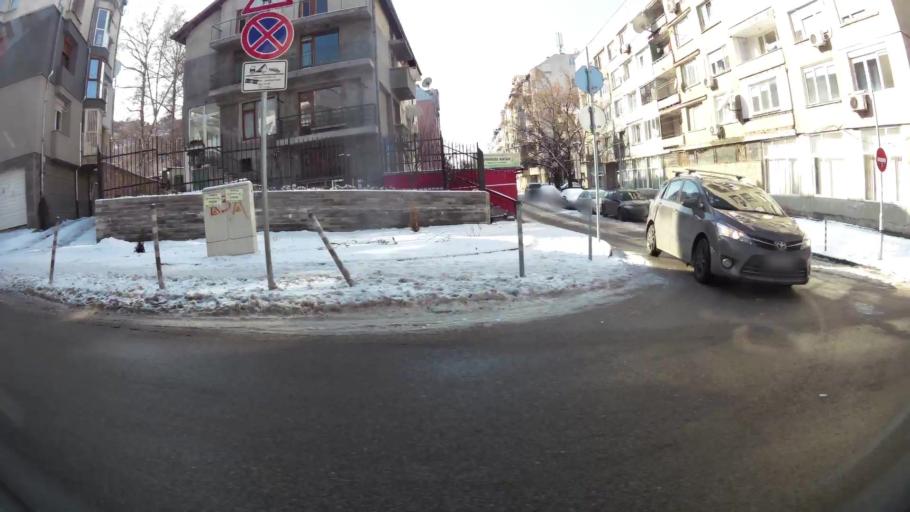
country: BG
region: Sofia-Capital
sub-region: Stolichna Obshtina
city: Sofia
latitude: 42.6732
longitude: 23.3129
